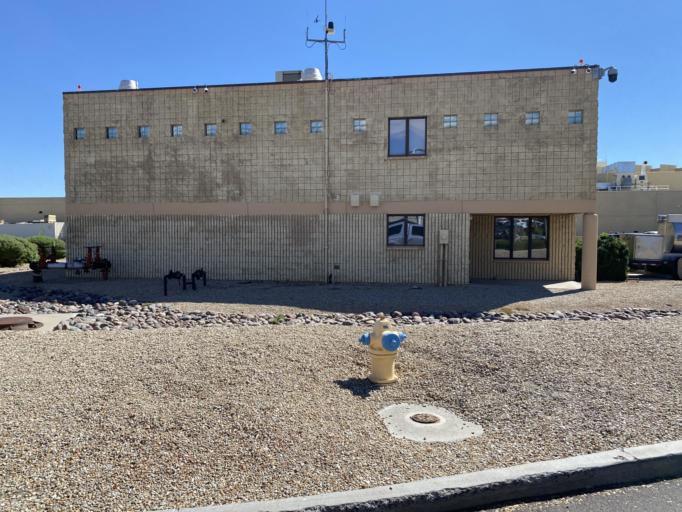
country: US
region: Arizona
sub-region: Mohave County
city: Kingman
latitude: 35.2209
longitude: -114.0381
